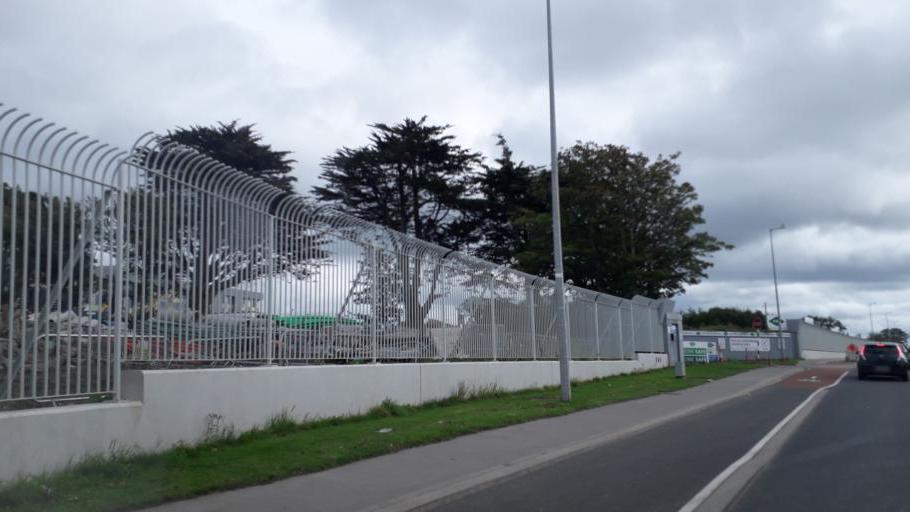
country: IE
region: Leinster
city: Cabinteely
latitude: 53.2748
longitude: -6.1546
